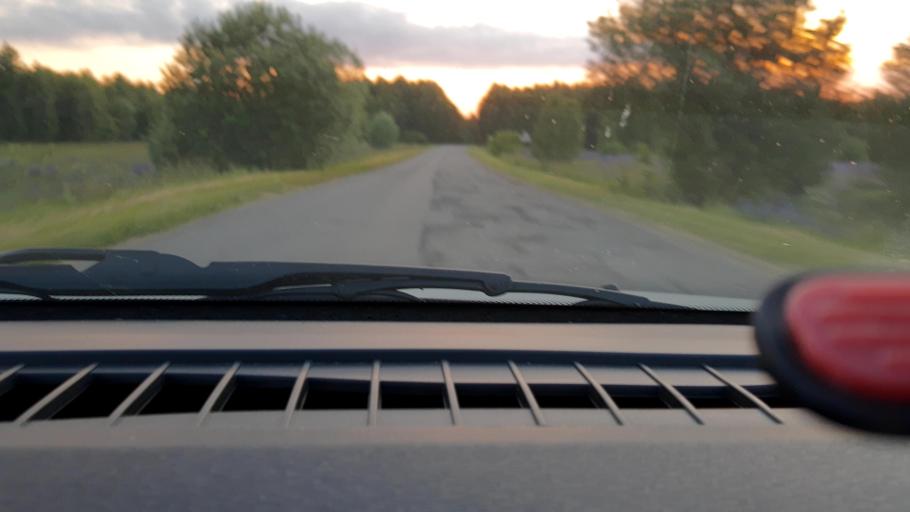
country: RU
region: Nizjnij Novgorod
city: Surovatikha
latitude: 55.8510
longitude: 43.9402
